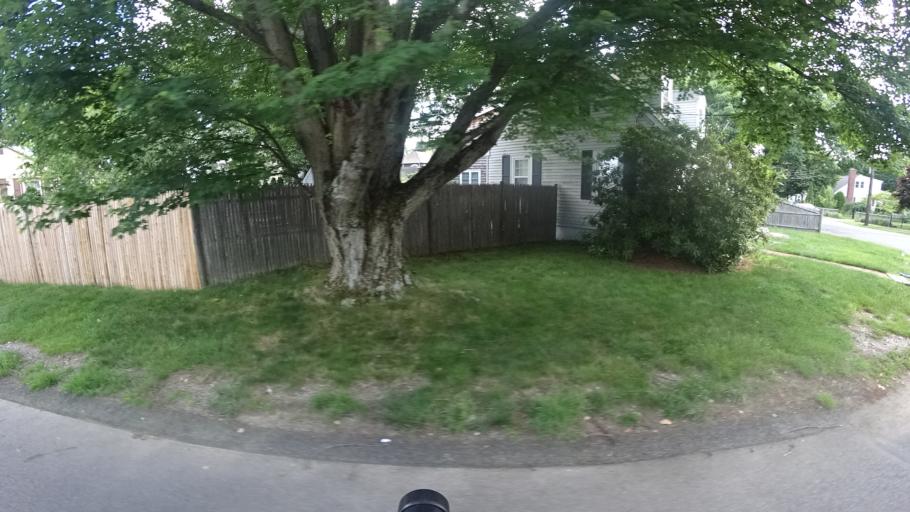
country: US
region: Massachusetts
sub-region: Norfolk County
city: Dedham
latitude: 42.2748
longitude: -71.1806
